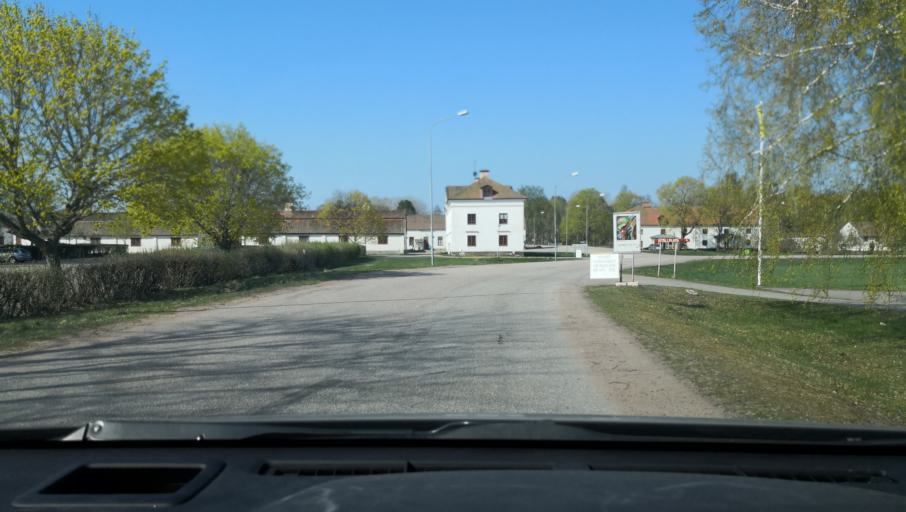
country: SE
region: Uppsala
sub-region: Heby Kommun
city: Tarnsjo
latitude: 60.2880
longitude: 16.8845
